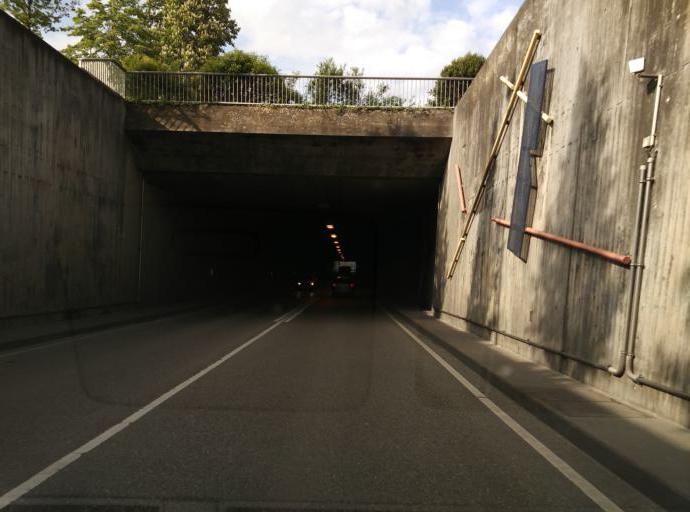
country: DE
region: Baden-Wuerttemberg
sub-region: Regierungsbezirk Stuttgart
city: Neckartailfingen
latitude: 48.6098
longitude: 9.2641
